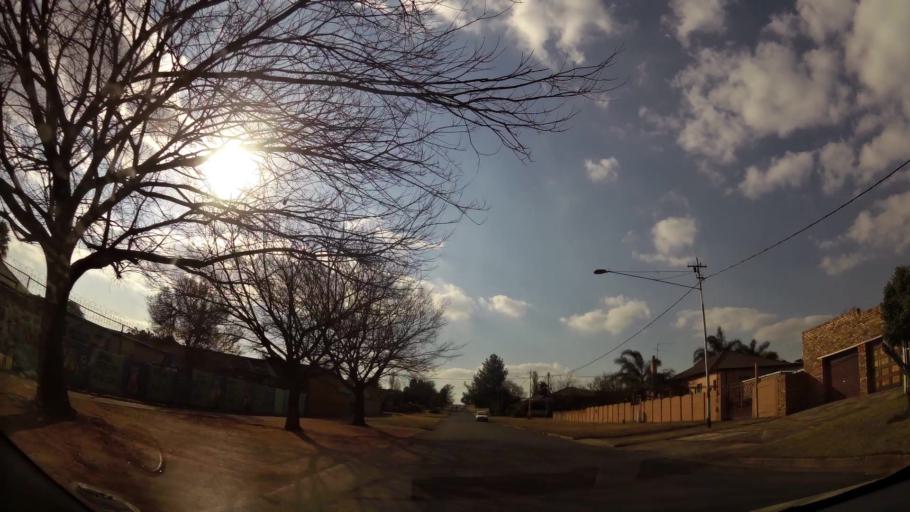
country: ZA
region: Gauteng
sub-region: West Rand District Municipality
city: Krugersdorp
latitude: -26.0875
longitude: 27.7654
